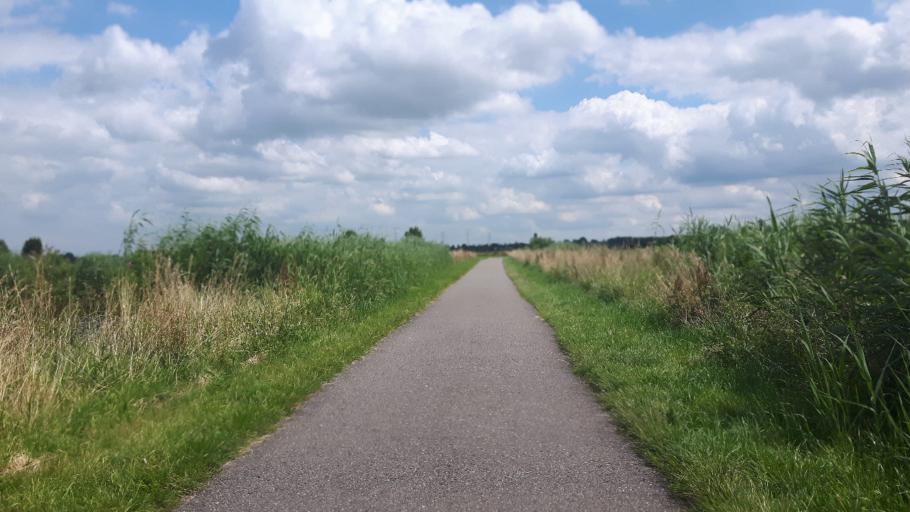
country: NL
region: South Holland
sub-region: Gemeente Krimpen aan den IJssel
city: Krimpen aan den IJssel
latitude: 51.9046
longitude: 4.6143
